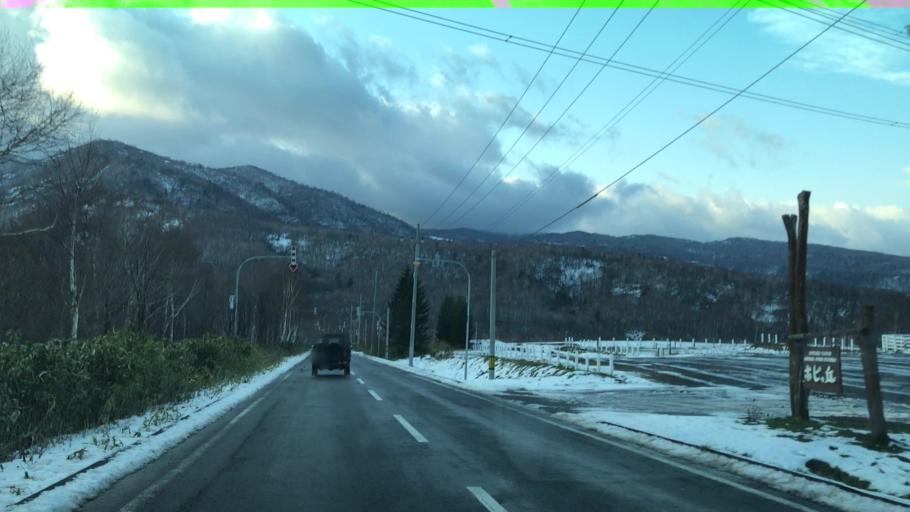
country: JP
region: Hokkaido
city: Otaru
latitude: 43.0906
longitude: 140.9746
